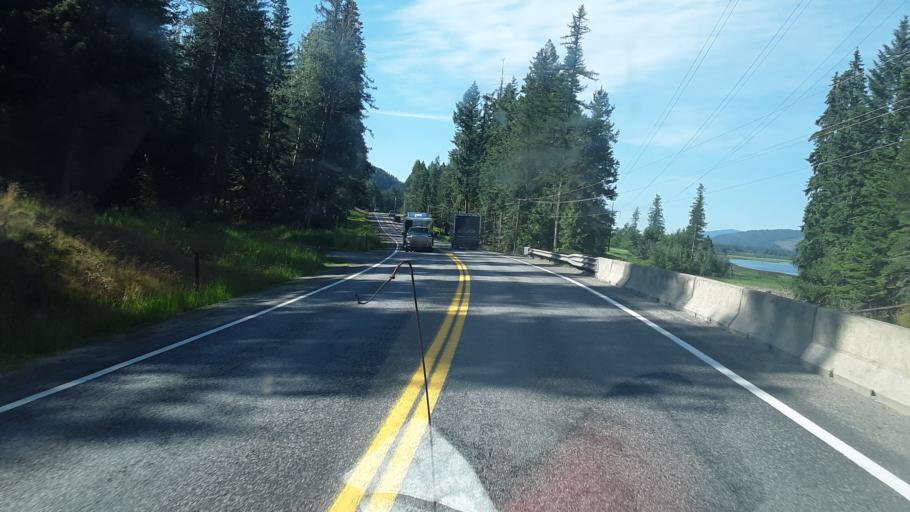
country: US
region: Idaho
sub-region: Boundary County
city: Bonners Ferry
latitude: 48.5181
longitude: -116.4435
